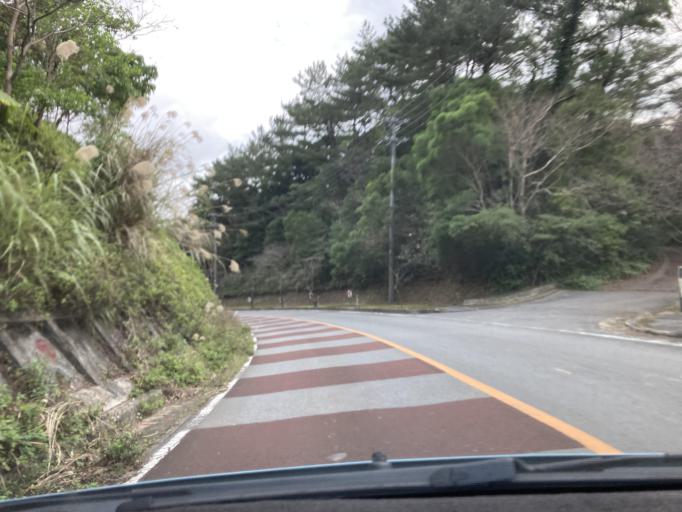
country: JP
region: Okinawa
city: Nago
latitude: 26.8313
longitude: 128.2724
